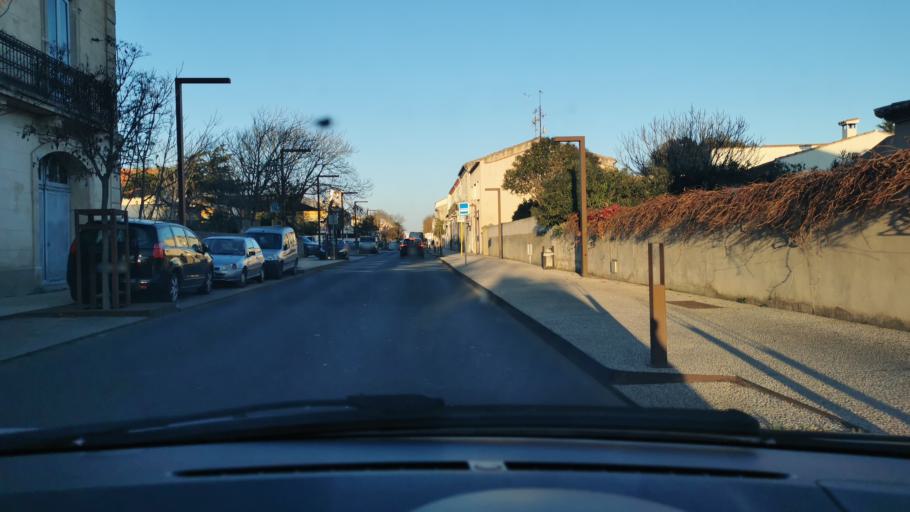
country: FR
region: Languedoc-Roussillon
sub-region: Departement de l'Herault
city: Frontignan
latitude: 43.4451
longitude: 3.7516
